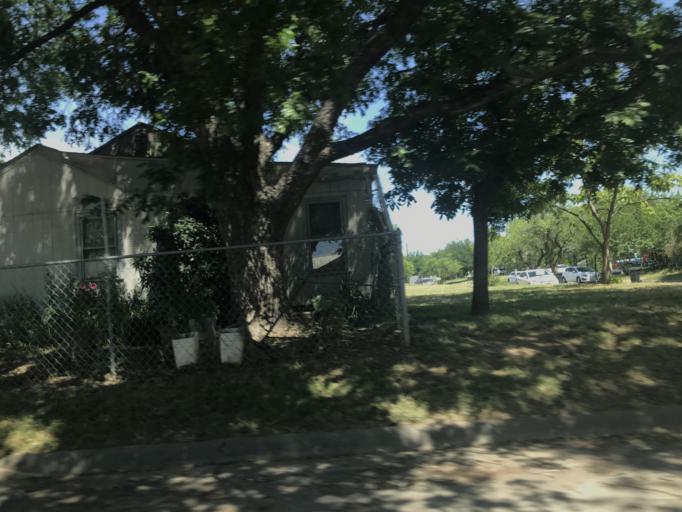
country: US
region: Texas
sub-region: Taylor County
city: Abilene
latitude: 32.4361
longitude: -99.7614
